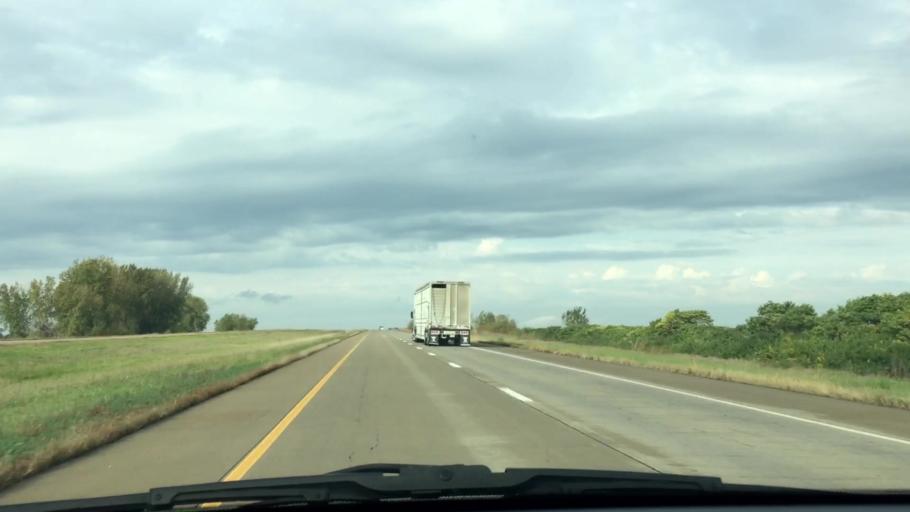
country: US
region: Illinois
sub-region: Whiteside County
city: Sterling
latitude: 41.7657
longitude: -89.8268
